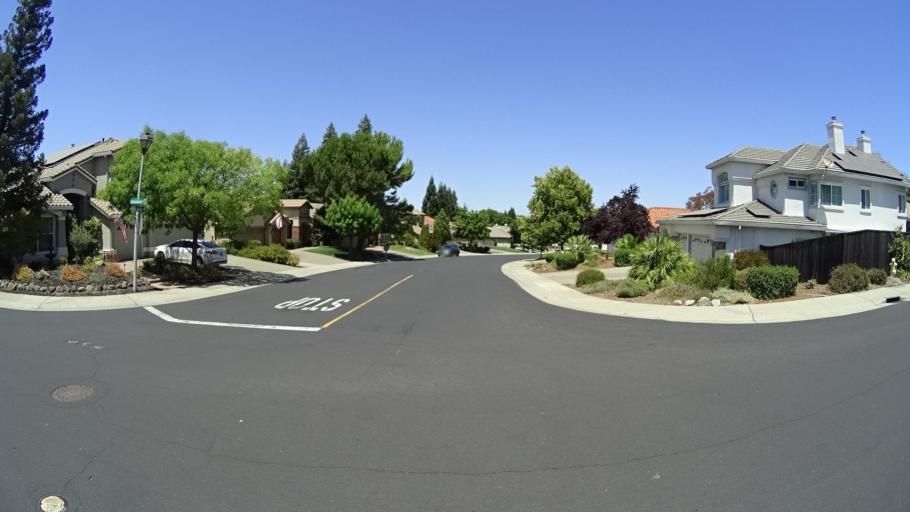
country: US
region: California
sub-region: Placer County
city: Rocklin
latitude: 38.8221
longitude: -121.2483
